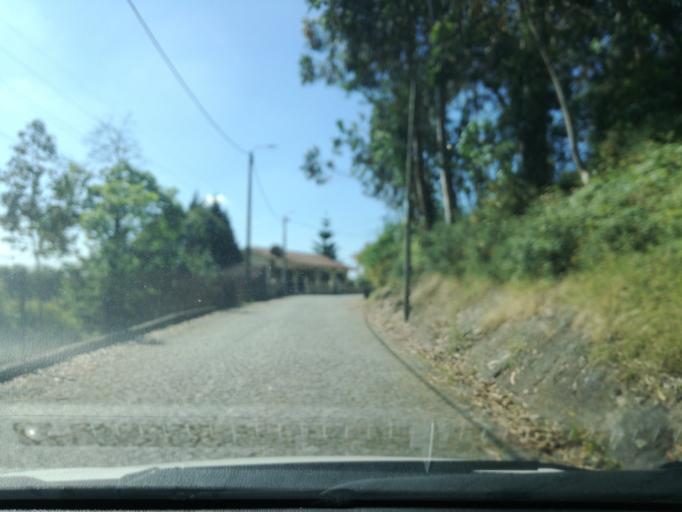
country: PT
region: Porto
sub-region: Maia
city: Nogueira
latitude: 41.2475
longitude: -8.6022
